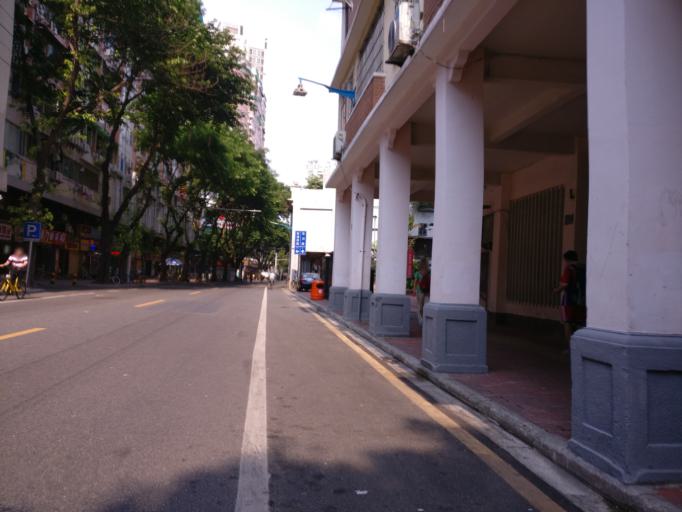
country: CN
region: Guangdong
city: Guangzhou
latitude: 23.1247
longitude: 113.2766
